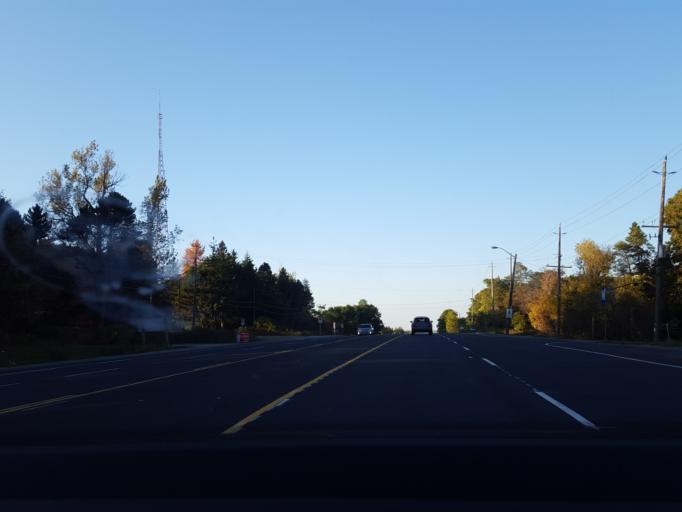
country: CA
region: Ontario
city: Newmarket
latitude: 43.9648
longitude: -79.4592
